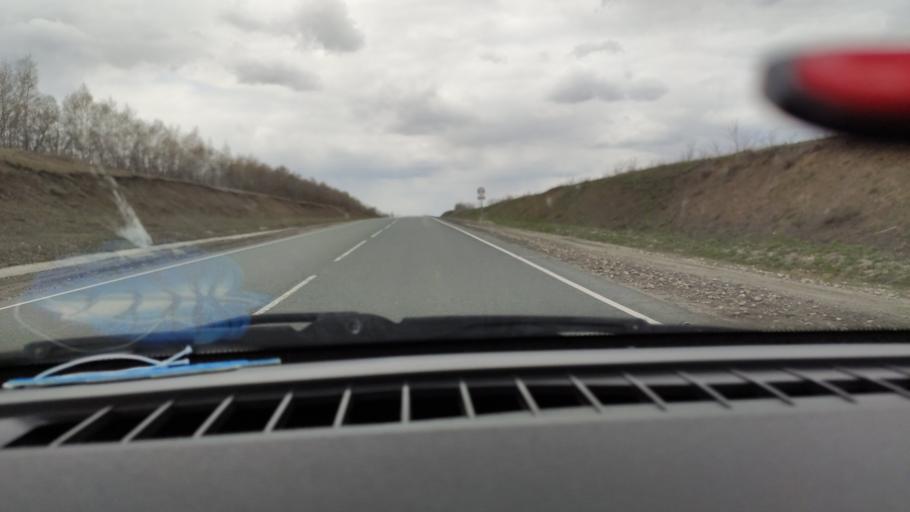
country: RU
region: Saratov
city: Shikhany
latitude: 52.1167
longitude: 47.2820
